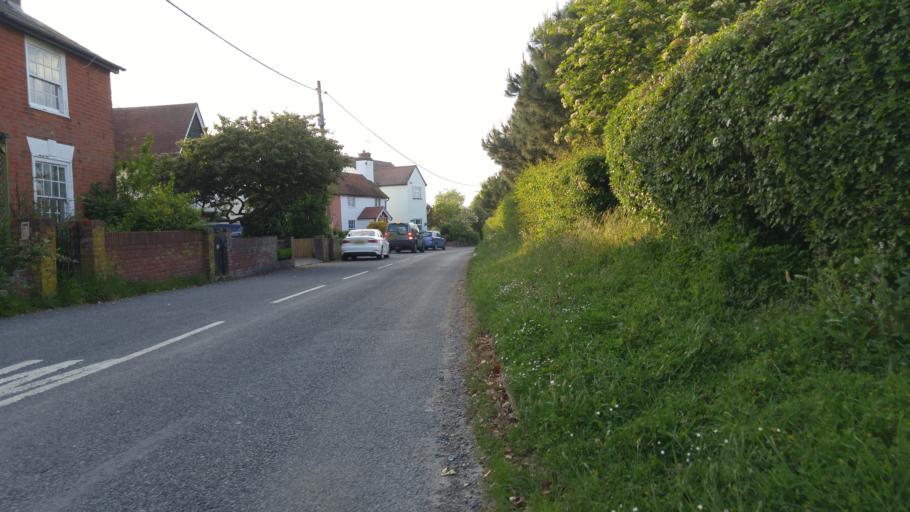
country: GB
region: England
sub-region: Essex
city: Tiptree
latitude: 51.8353
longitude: 0.7500
